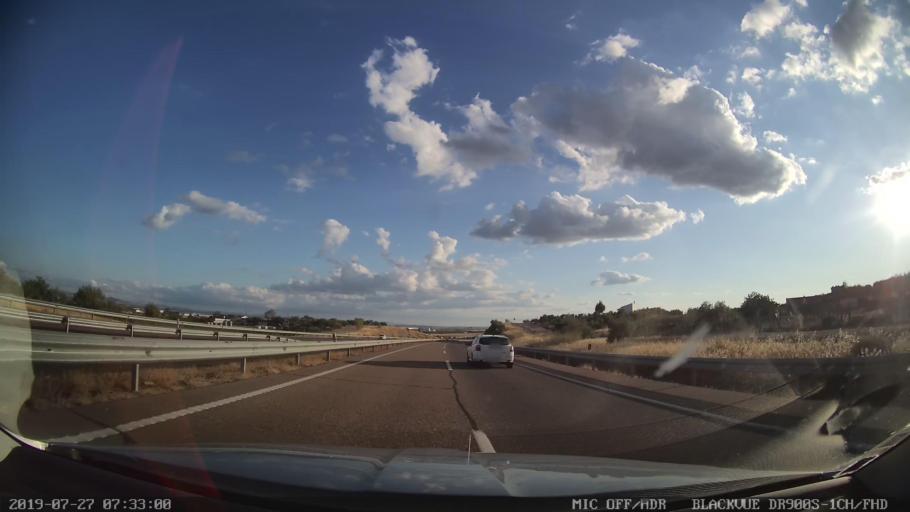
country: ES
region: Extremadura
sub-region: Provincia de Caceres
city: Miajadas
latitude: 39.1492
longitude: -5.9291
